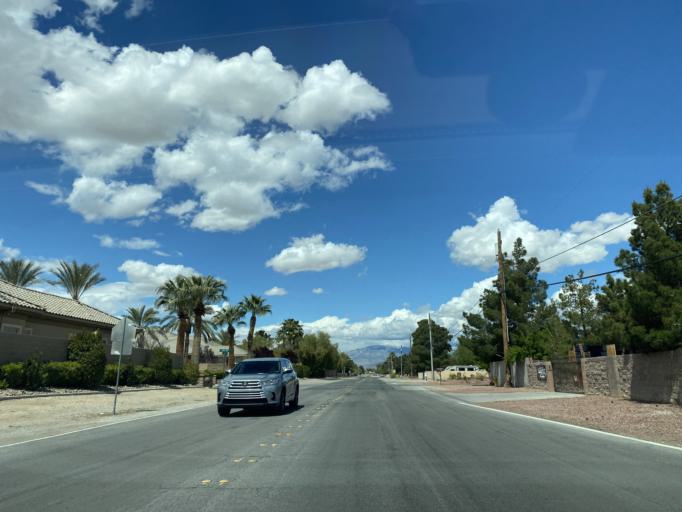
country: US
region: Nevada
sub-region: Clark County
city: Spring Valley
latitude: 36.2452
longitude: -115.2698
